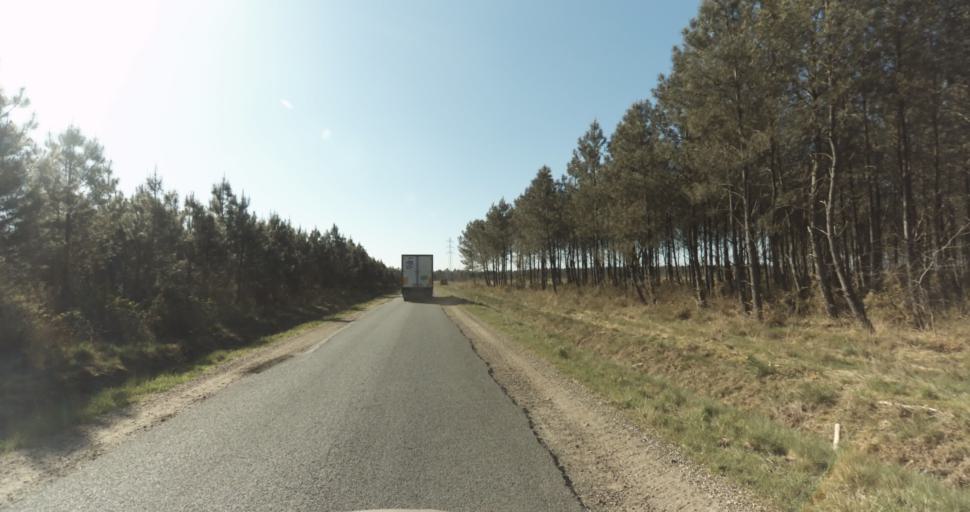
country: FR
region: Aquitaine
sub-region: Departement de la Gironde
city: Marcheprime
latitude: 44.7533
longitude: -0.8491
